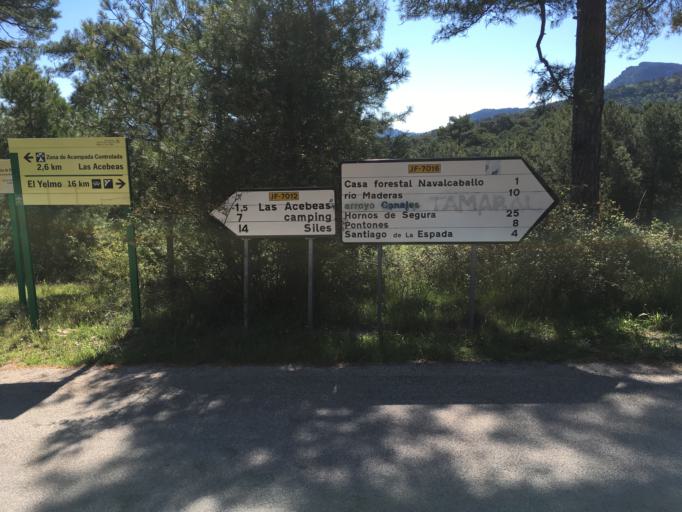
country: ES
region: Andalusia
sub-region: Provincia de Jaen
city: Segura de la Sierra
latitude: 38.3104
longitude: -2.5824
